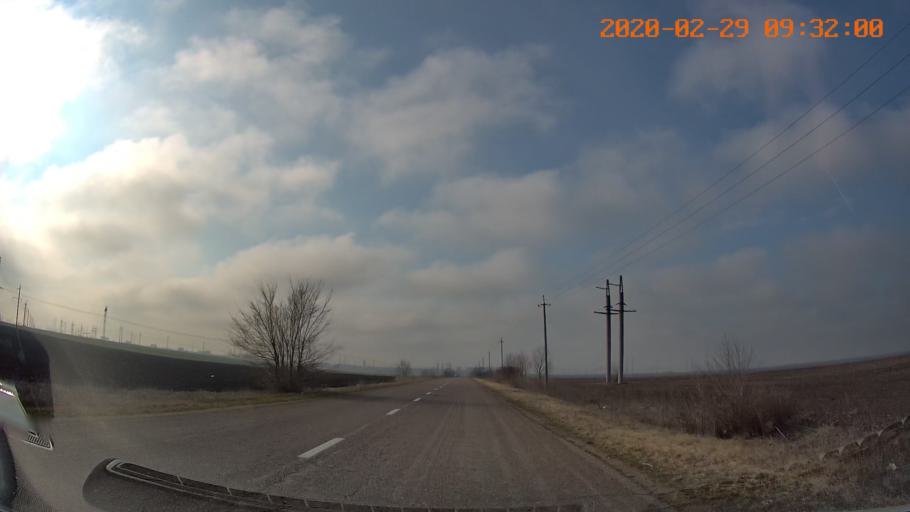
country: MD
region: Telenesti
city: Dnestrovsc
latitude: 46.6451
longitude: 29.9082
